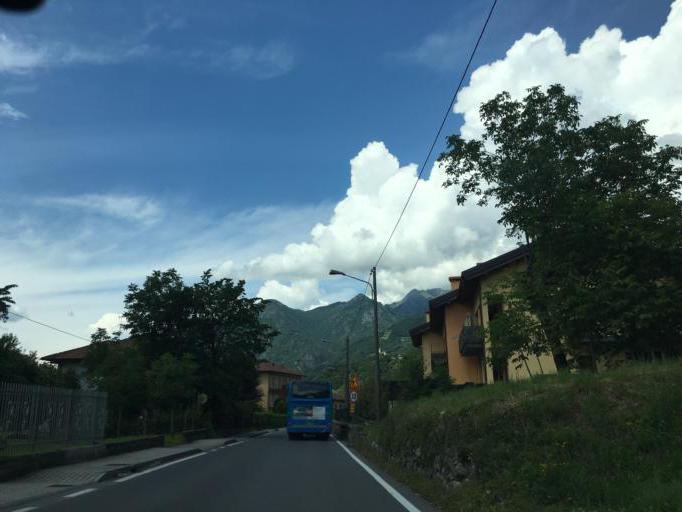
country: IT
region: Lombardy
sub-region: Provincia di Como
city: Carlazzo
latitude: 46.0421
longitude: 9.1660
